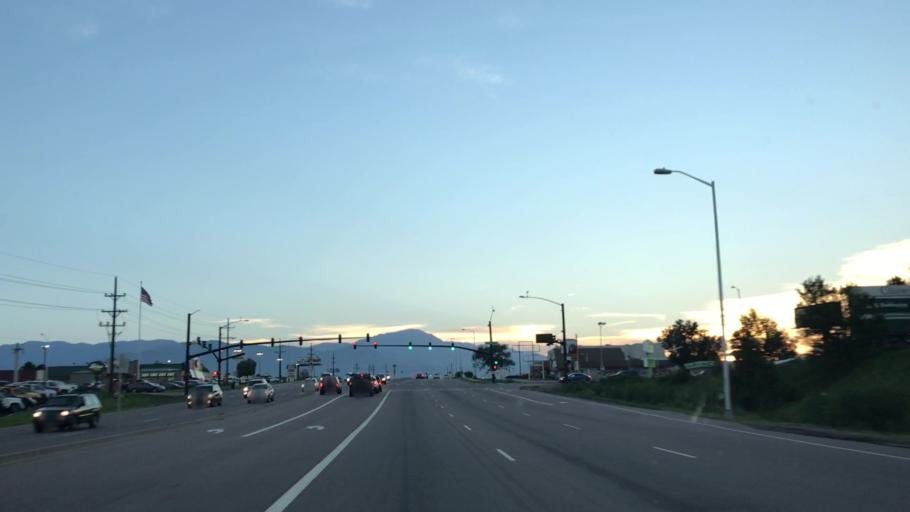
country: US
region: Colorado
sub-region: El Paso County
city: Colorado Springs
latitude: 38.8398
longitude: -104.7653
